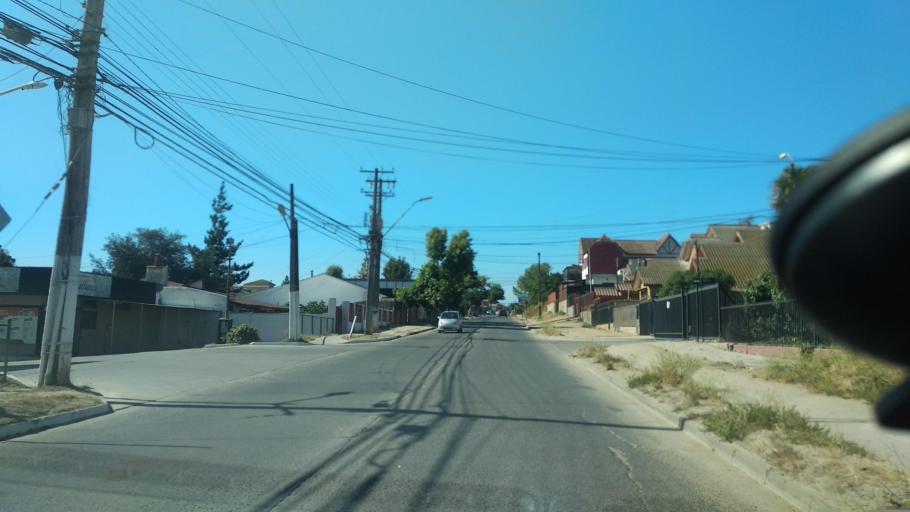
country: CL
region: Valparaiso
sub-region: Provincia de Marga Marga
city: Villa Alemana
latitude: -33.0521
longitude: -71.3742
